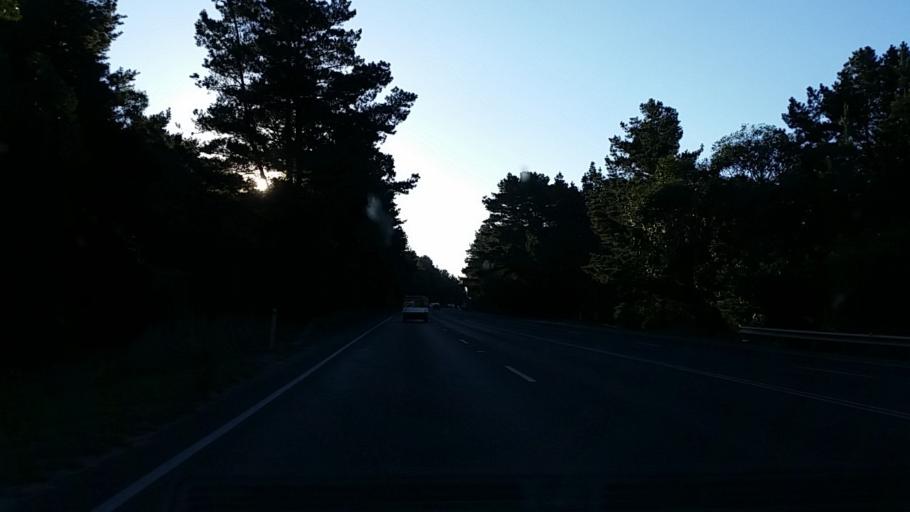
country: AU
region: South Australia
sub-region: Alexandrina
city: Mount Compass
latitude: -35.3365
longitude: 138.5943
